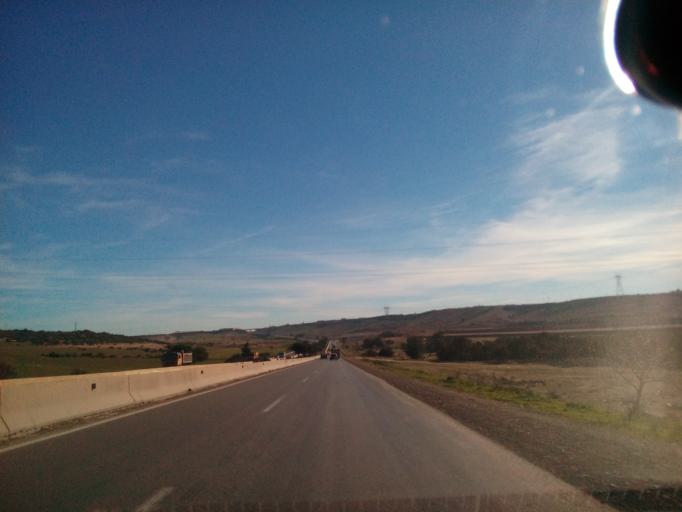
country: DZ
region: Oran
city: Ain el Bya
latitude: 35.7710
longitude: -0.2414
